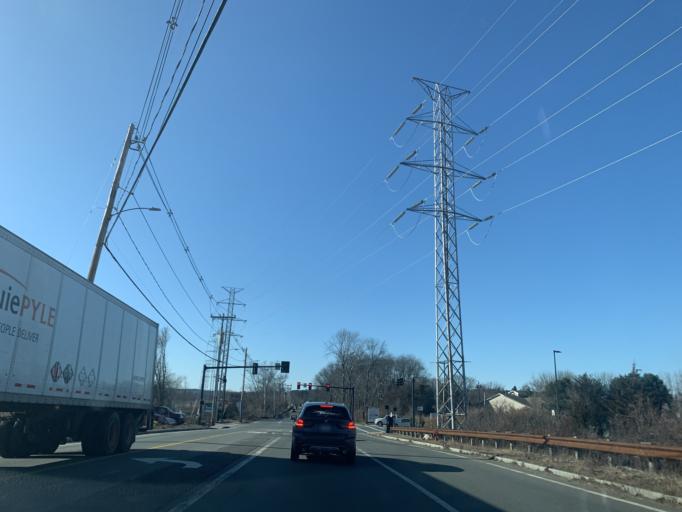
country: US
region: Massachusetts
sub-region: Middlesex County
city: Wayland
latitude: 42.3633
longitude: -71.3695
